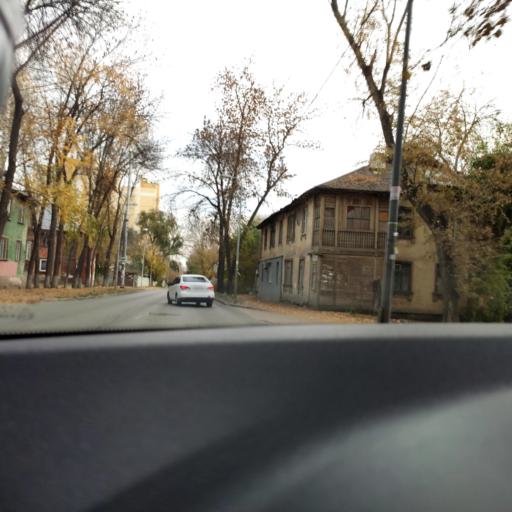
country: RU
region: Samara
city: Samara
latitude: 53.2392
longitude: 50.2593
